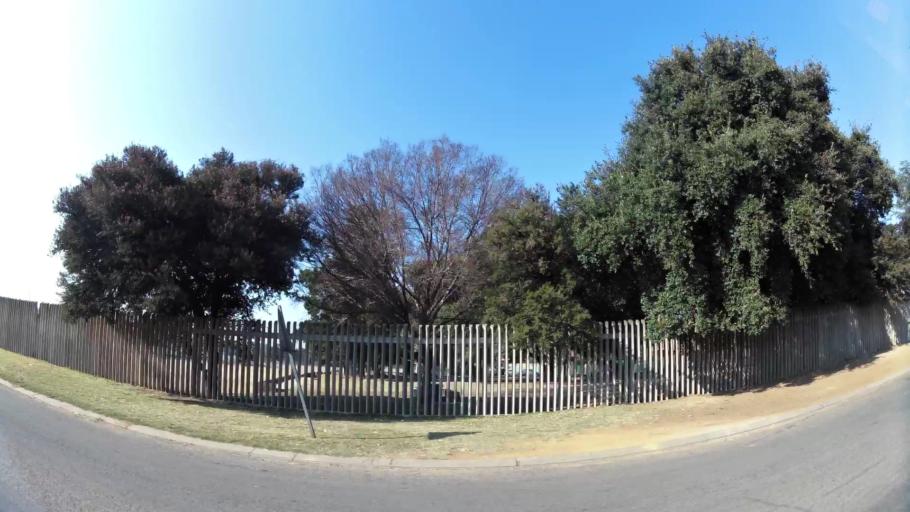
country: ZA
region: Gauteng
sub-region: Ekurhuleni Metropolitan Municipality
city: Boksburg
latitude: -26.2340
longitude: 28.2333
